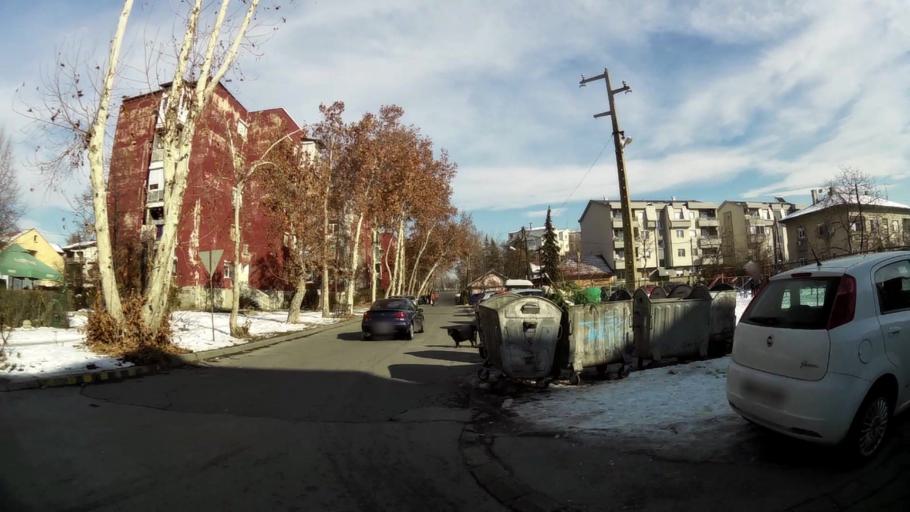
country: MK
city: Krushopek
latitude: 42.0028
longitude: 21.3719
